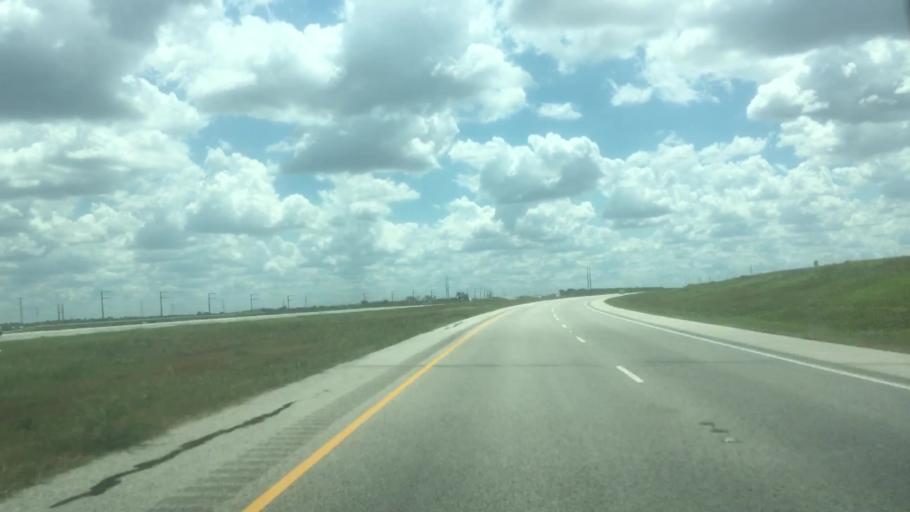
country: US
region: Texas
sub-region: Caldwell County
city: Uhland
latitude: 30.0216
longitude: -97.6876
